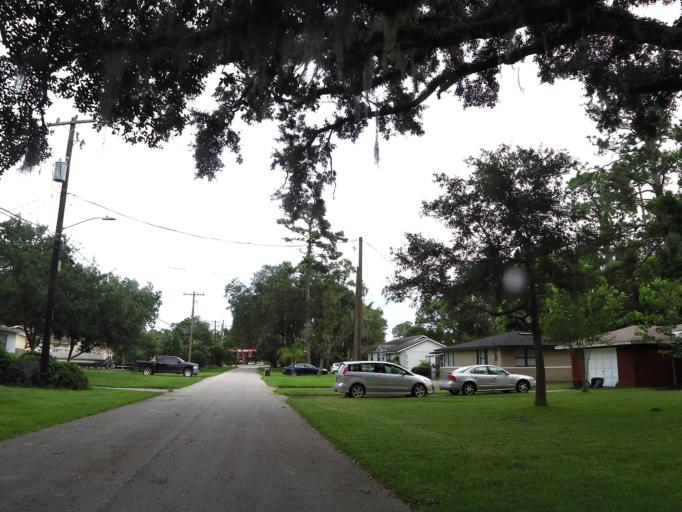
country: US
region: Florida
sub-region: Duval County
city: Jacksonville
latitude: 30.3100
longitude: -81.6182
